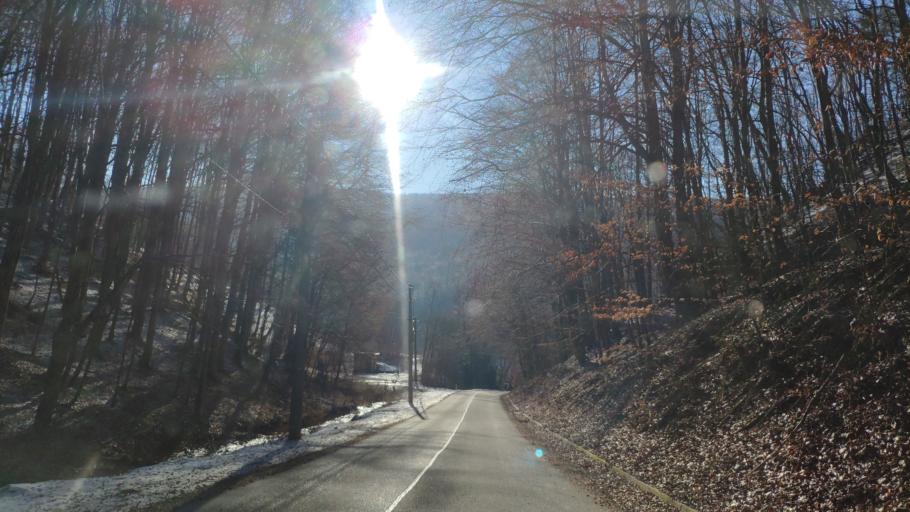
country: SK
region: Kosicky
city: Medzev
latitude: 48.7496
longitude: 21.0044
